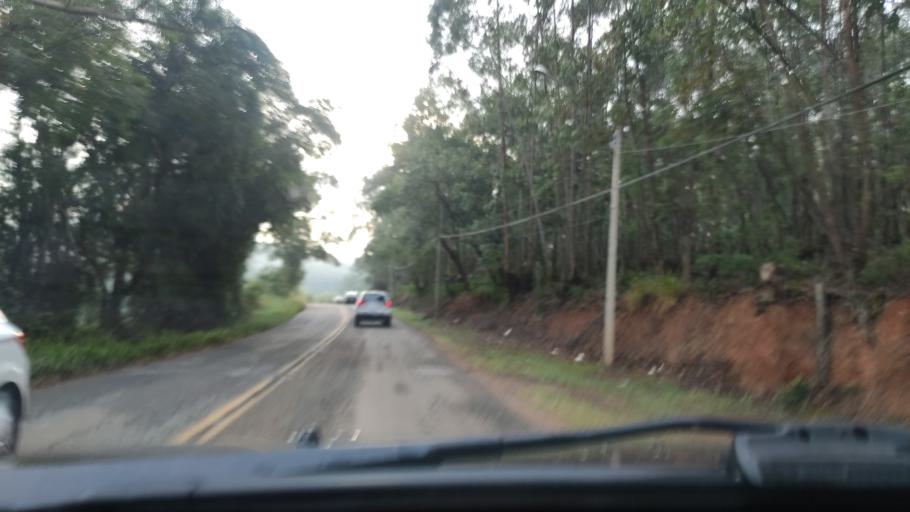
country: BR
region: Sao Paulo
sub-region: Jarinu
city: Jarinu
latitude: -23.1217
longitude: -46.7695
